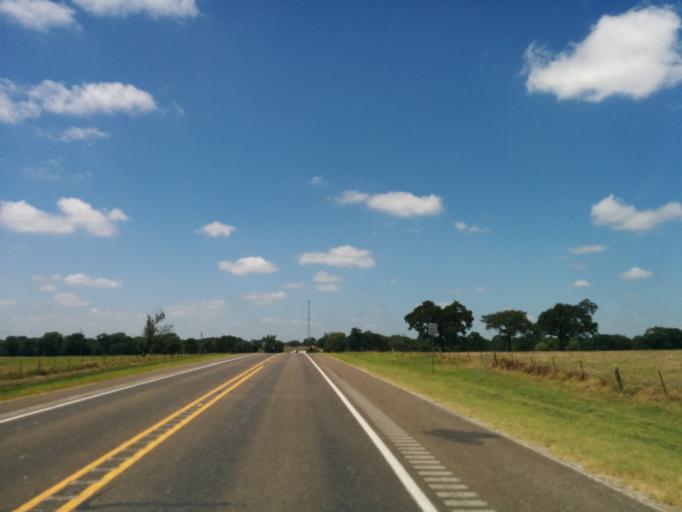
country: US
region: Texas
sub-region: Madison County
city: Madisonville
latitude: 30.9216
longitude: -96.0761
